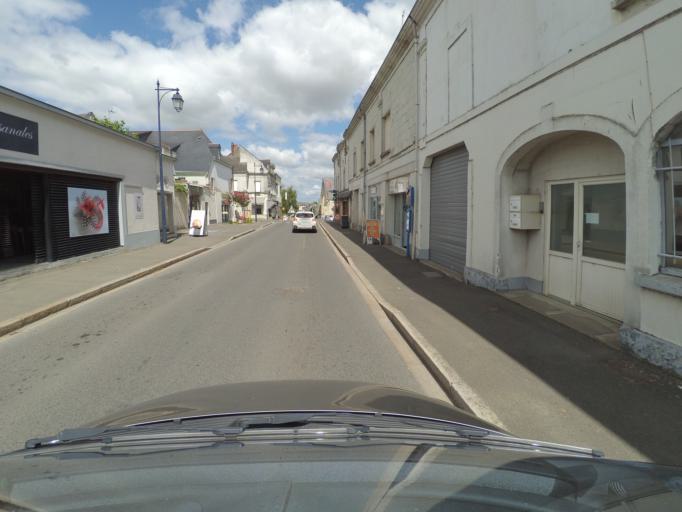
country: FR
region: Pays de la Loire
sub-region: Departement de Maine-et-Loire
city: Les Rosiers-sur-Loire
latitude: 47.3499
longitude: -0.2265
